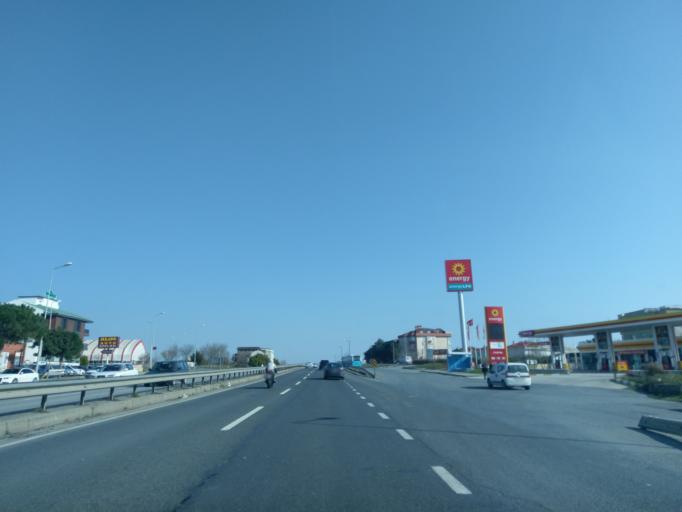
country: TR
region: Istanbul
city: Selimpasa
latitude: 41.0504
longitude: 28.3904
